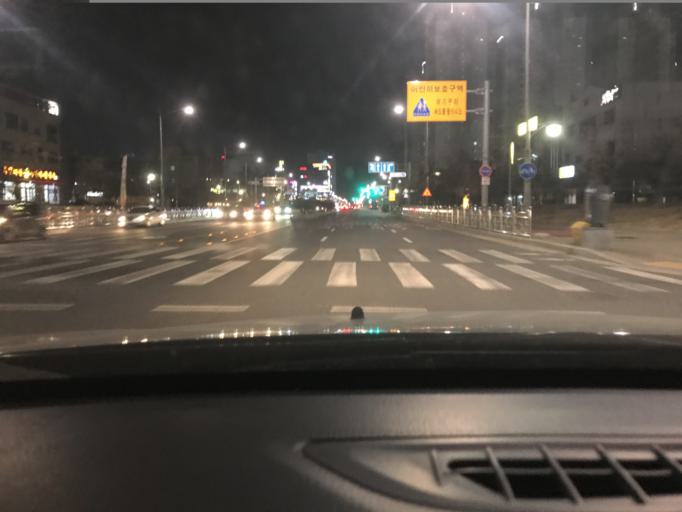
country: KR
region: Daegu
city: Hwawon
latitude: 35.6987
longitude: 128.4577
